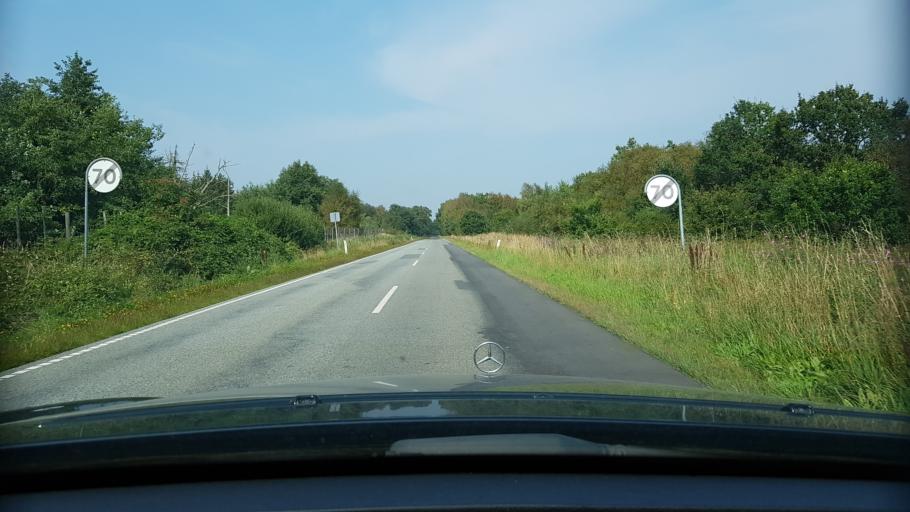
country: DK
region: North Denmark
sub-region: Alborg Kommune
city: Hals
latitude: 56.8323
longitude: 10.2682
